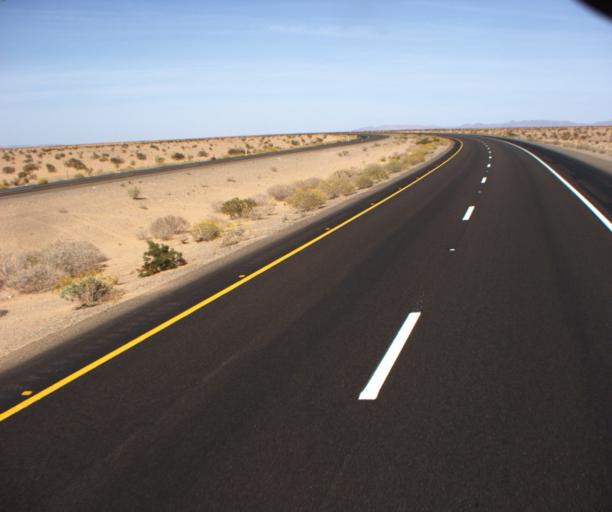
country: US
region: Arizona
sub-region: Yuma County
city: Somerton
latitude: 32.4982
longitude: -114.5617
